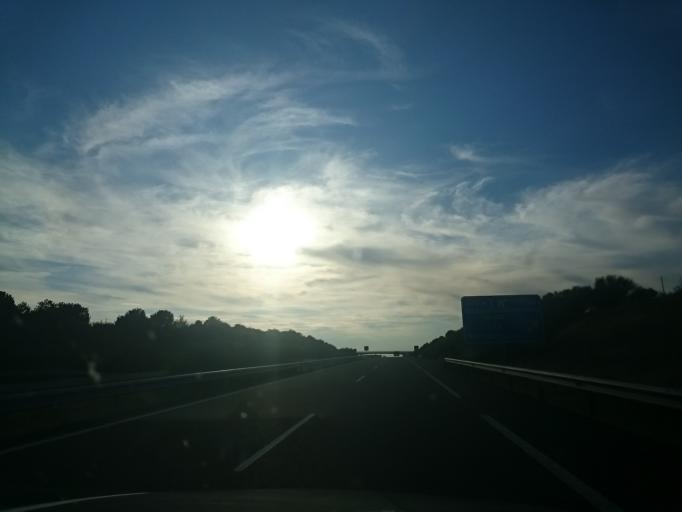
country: ES
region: Castille and Leon
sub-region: Provincia de Leon
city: Sahagun
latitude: 42.3801
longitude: -5.0160
